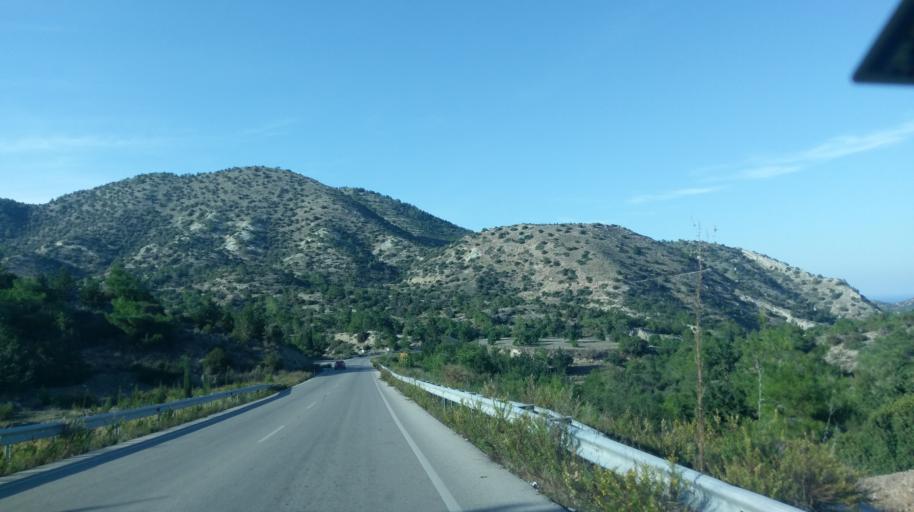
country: CY
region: Ammochostos
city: Lefkonoiko
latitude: 35.3387
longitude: 33.7132
